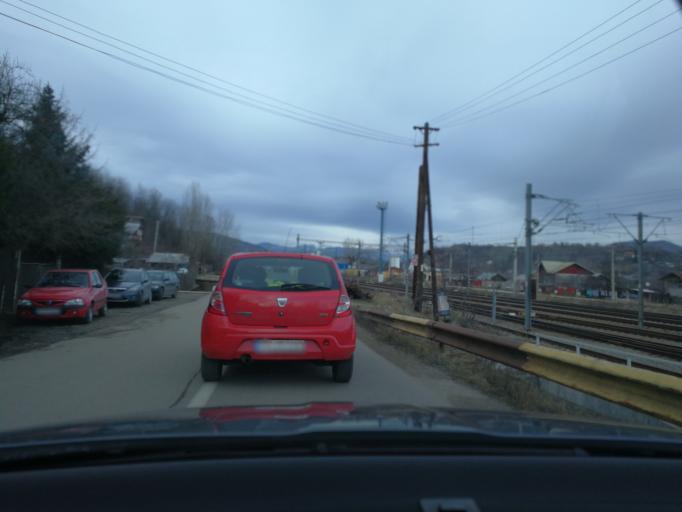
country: RO
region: Prahova
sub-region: Comuna Cornu
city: Cornu de Jos
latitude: 45.1355
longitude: 25.7053
